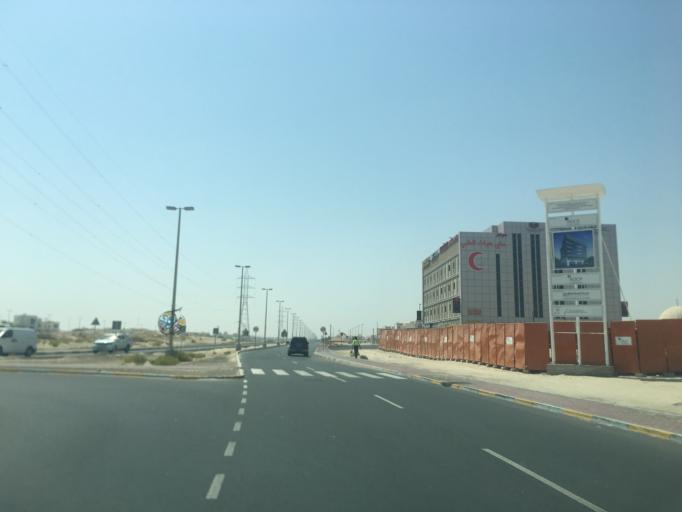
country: AE
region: Abu Dhabi
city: Abu Dhabi
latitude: 24.3188
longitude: 54.6309
